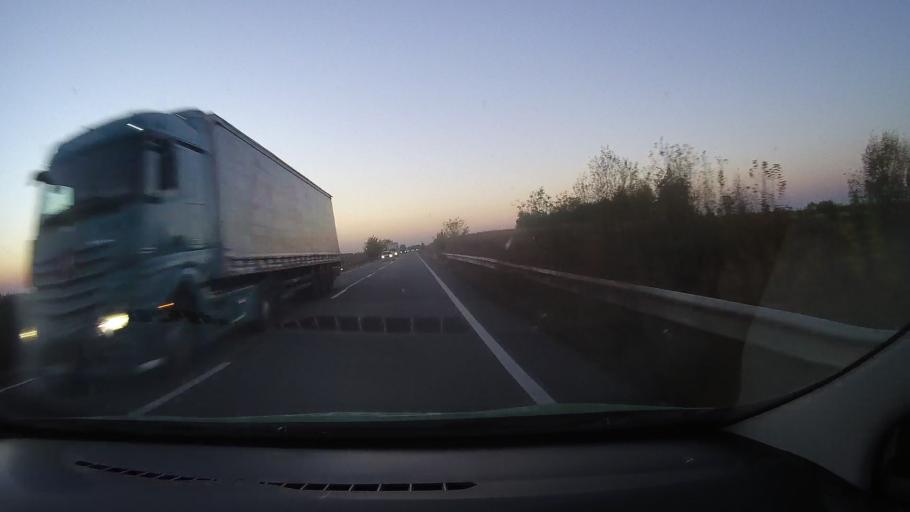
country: RO
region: Bihor
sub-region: Comuna Tarcea
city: Tarcea
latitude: 47.4357
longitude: 22.2012
